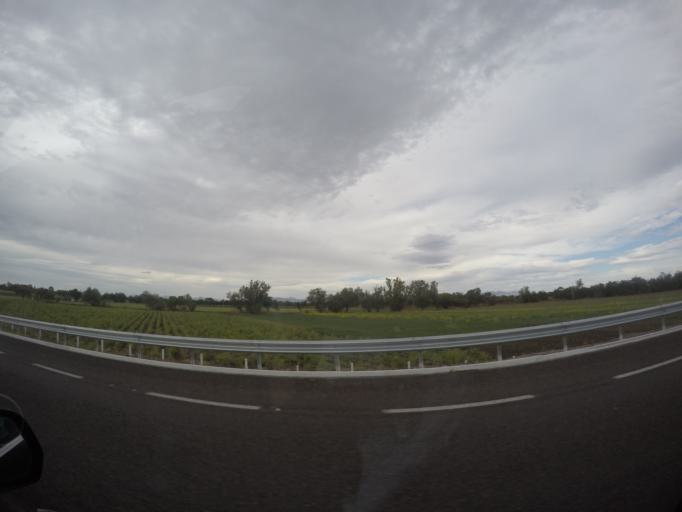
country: MX
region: Guanajuato
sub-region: Irapuato
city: Serrano
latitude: 20.7858
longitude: -101.4169
